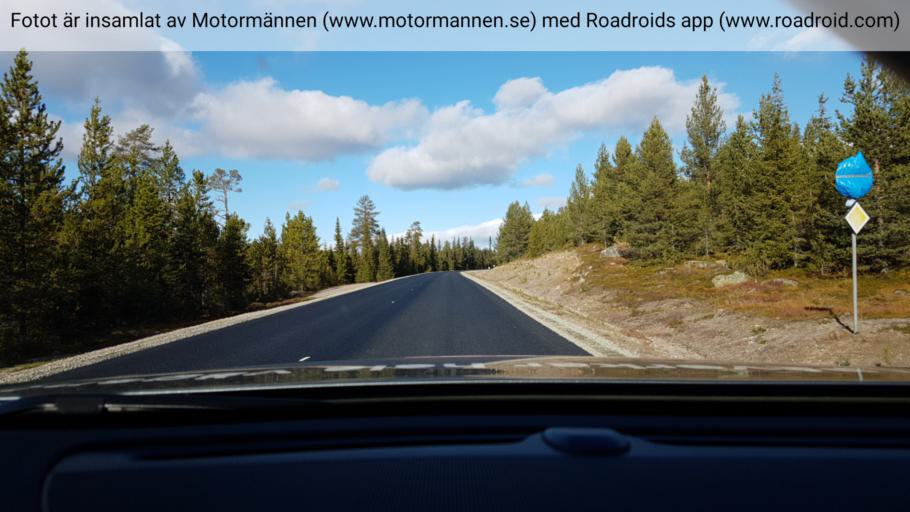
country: SE
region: Norrbotten
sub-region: Arjeplogs Kommun
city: Arjeplog
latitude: 65.9179
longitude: 18.3215
